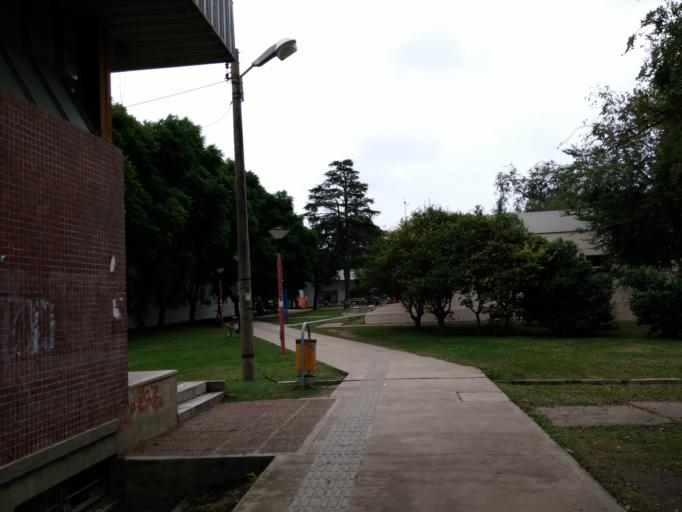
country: AR
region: Cordoba
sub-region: Departamento de Capital
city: Cordoba
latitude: -31.4398
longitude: -64.1882
